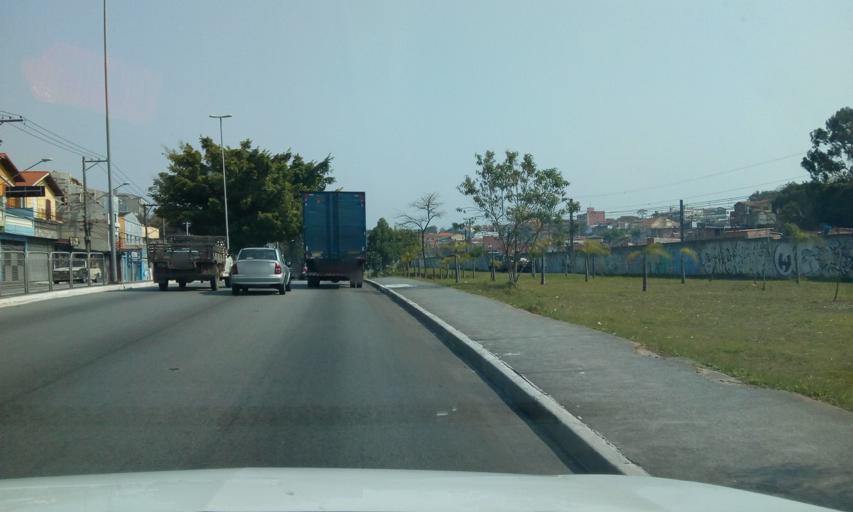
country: BR
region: Sao Paulo
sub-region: Diadema
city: Diadema
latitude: -23.7079
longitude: -46.6885
